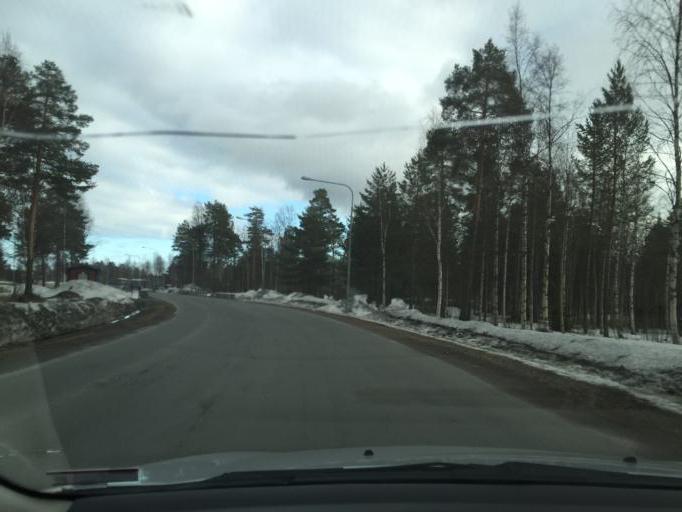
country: SE
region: Norrbotten
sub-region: Lulea Kommun
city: Lulea
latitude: 65.5912
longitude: 22.2253
